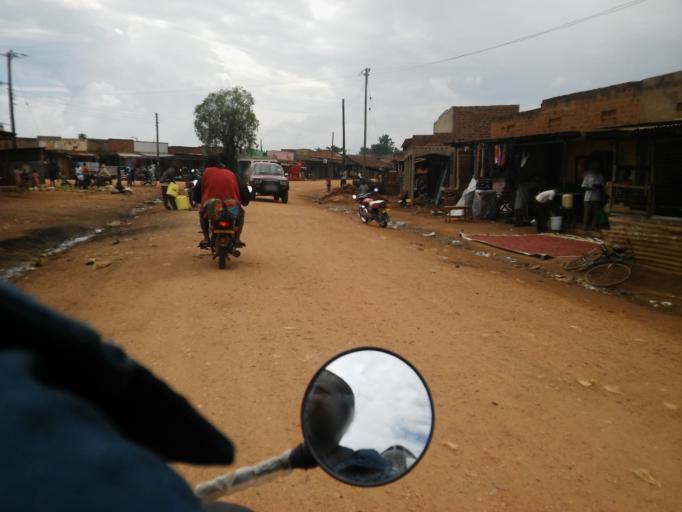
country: UG
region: Eastern Region
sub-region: Manafwa District
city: Manafwa
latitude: 0.8665
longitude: 34.3665
